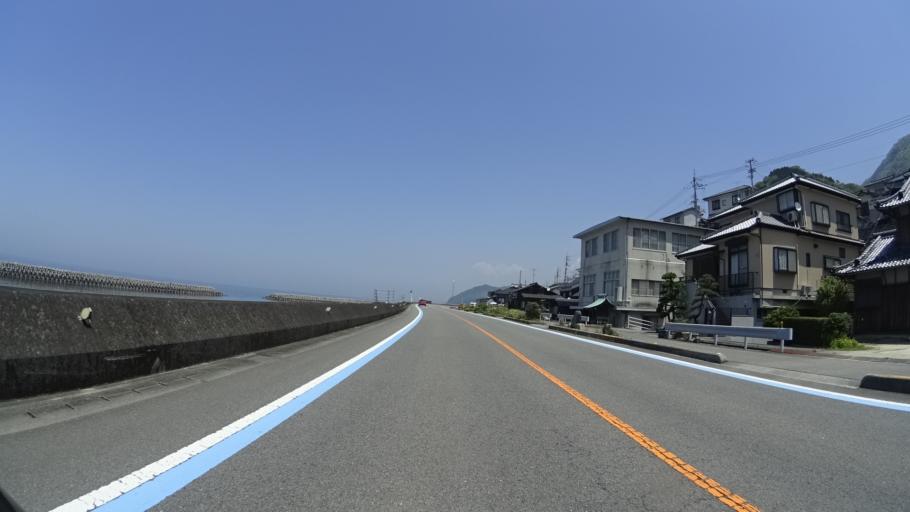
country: JP
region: Ehime
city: Iyo
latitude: 33.6936
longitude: 132.6486
